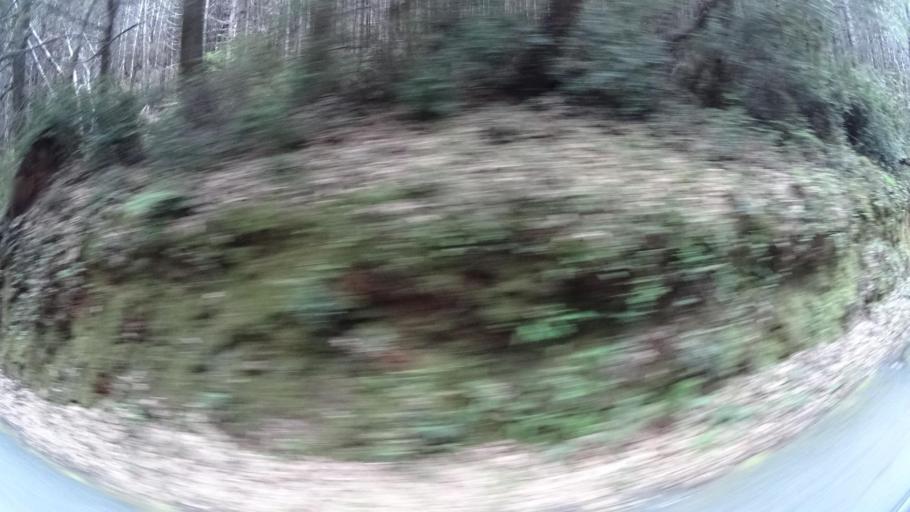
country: US
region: California
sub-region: Humboldt County
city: Willow Creek
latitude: 41.2009
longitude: -123.7608
